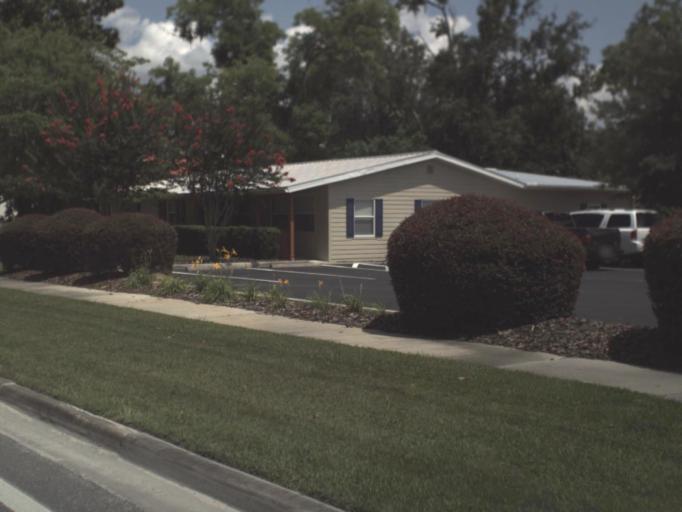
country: US
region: Florida
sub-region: Gilchrist County
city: Trenton
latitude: 29.6133
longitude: -82.8202
